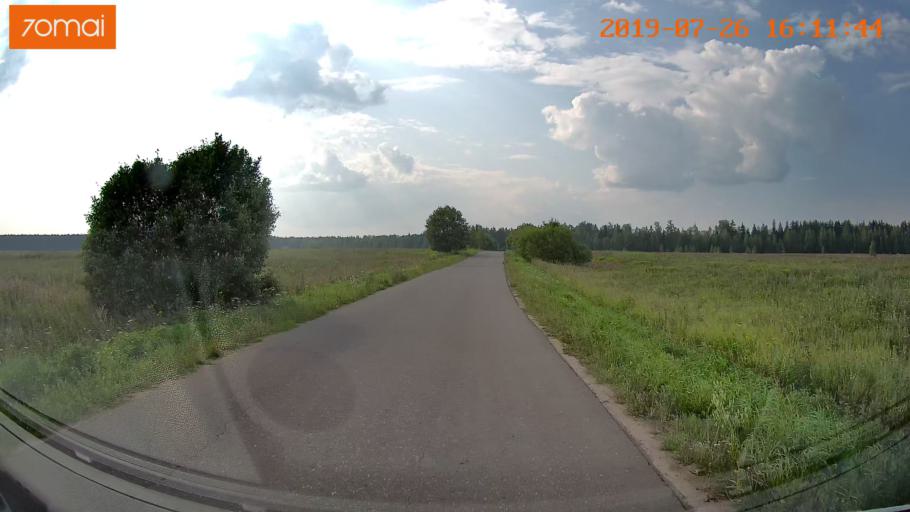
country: RU
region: Ivanovo
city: Bogorodskoye
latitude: 57.0666
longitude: 41.0563
